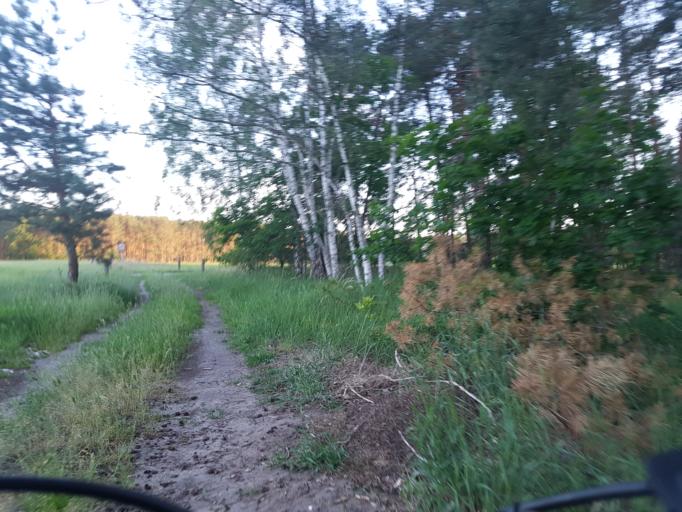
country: DE
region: Brandenburg
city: Bad Liebenwerda
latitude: 51.5568
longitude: 13.3800
